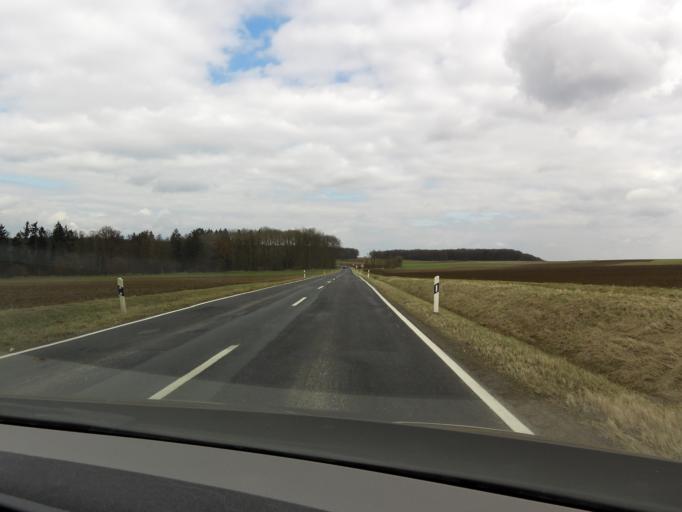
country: DE
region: Bavaria
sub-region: Regierungsbezirk Unterfranken
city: Arnstein
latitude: 49.9375
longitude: 9.9759
